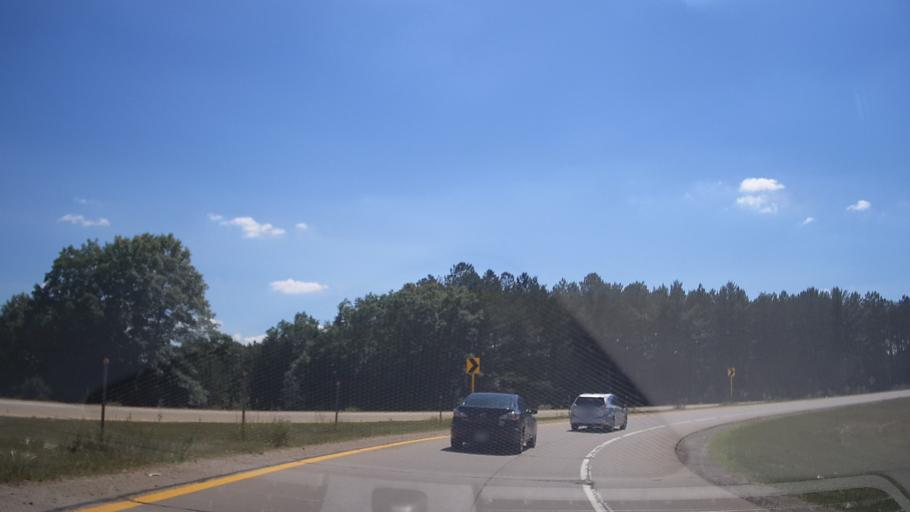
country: US
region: Michigan
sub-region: Clare County
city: Clare
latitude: 43.8634
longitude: -84.9093
